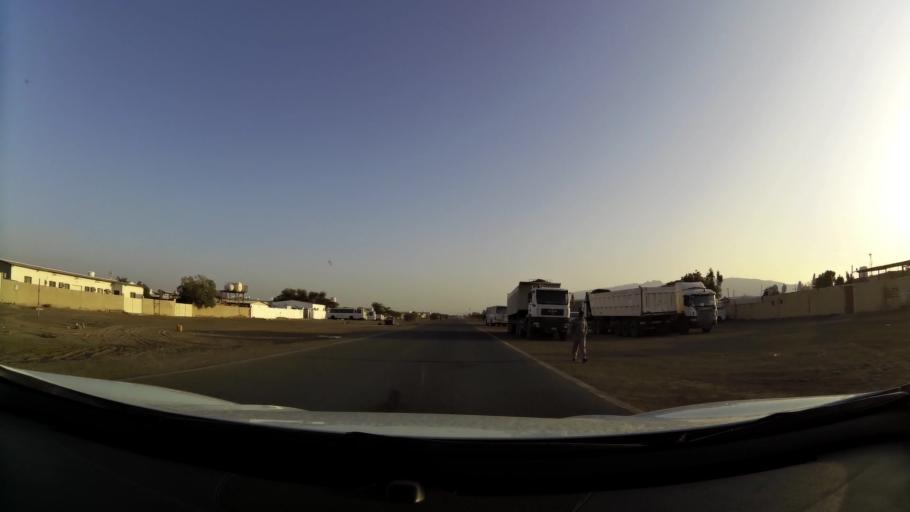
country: AE
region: Abu Dhabi
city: Al Ain
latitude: 24.1557
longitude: 55.8188
